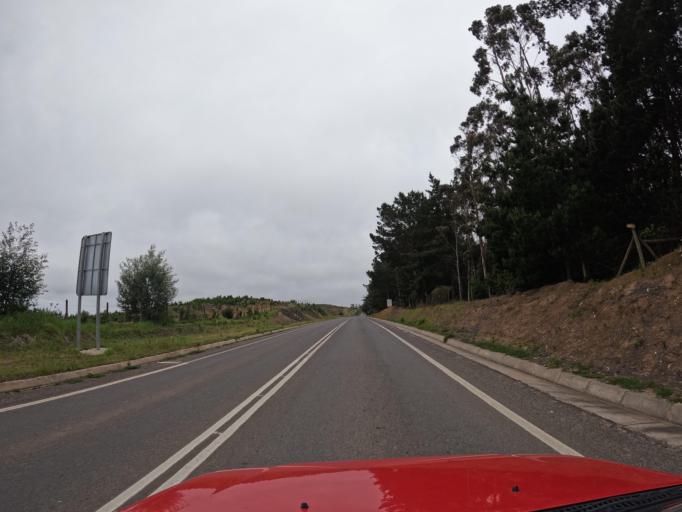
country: CL
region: O'Higgins
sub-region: Provincia de Colchagua
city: Santa Cruz
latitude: -34.6280
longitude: -72.0155
